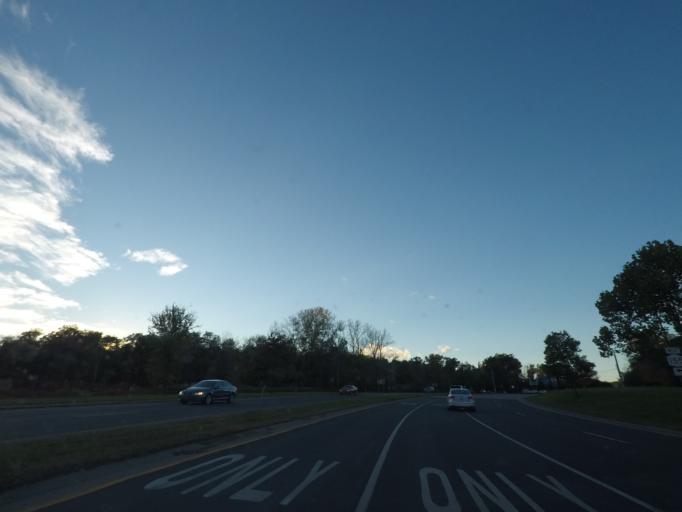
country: US
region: New York
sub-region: Albany County
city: Colonie
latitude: 42.7447
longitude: -73.8149
